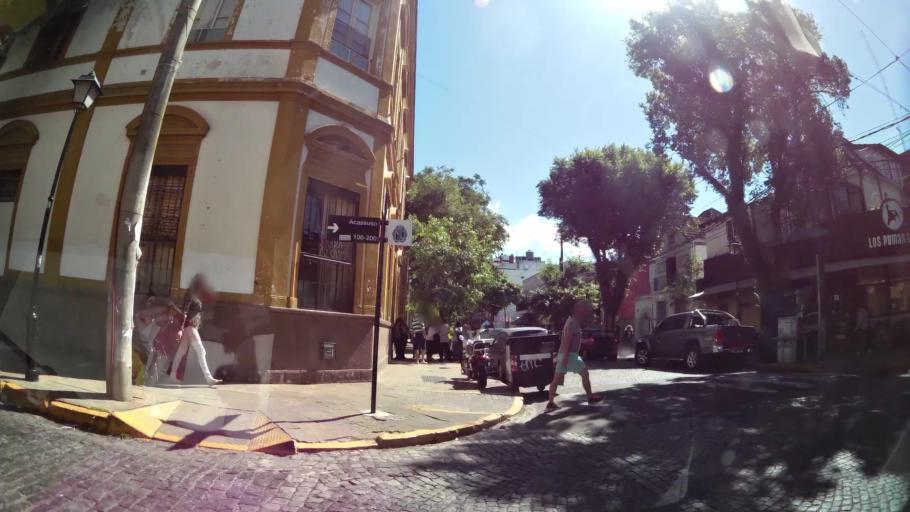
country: AR
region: Buenos Aires
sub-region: Partido de San Isidro
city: San Isidro
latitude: -34.4709
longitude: -58.5107
